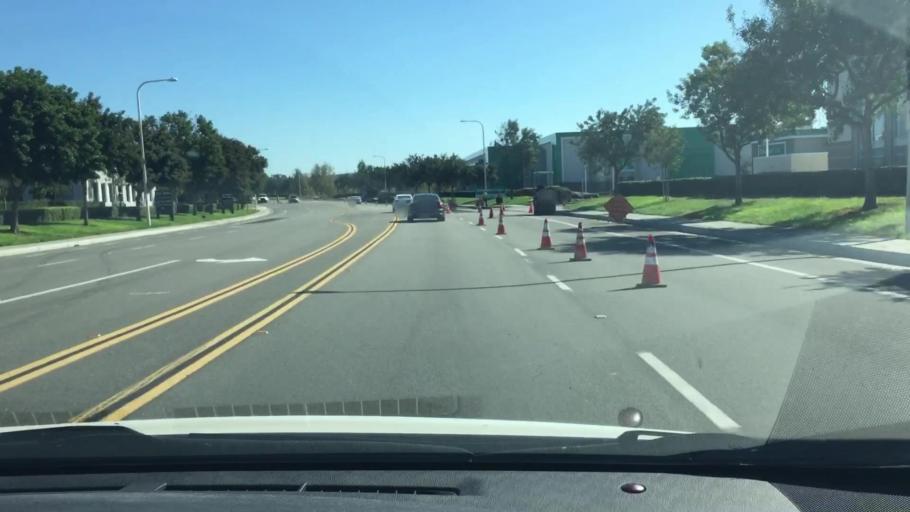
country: US
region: California
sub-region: Orange County
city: Laguna Woods
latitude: 33.6374
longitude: -117.7356
